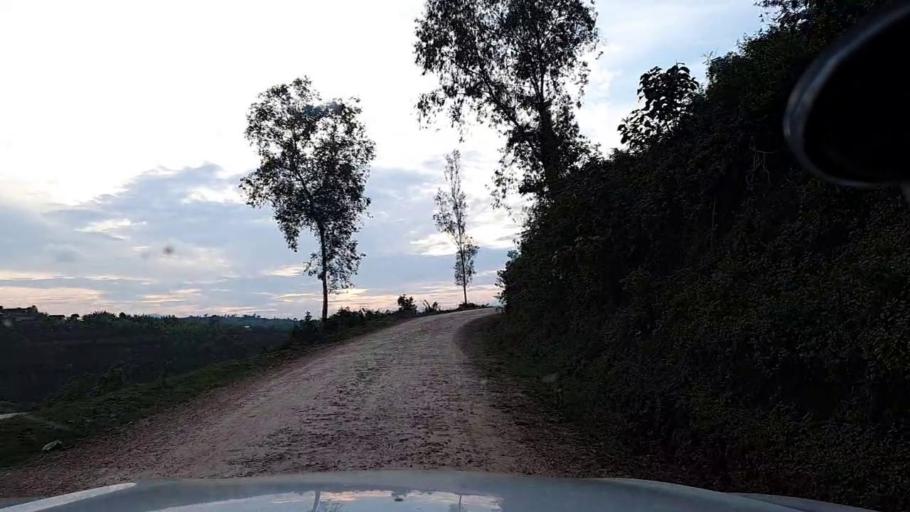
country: RW
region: Southern Province
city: Nyanza
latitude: -2.2143
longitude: 29.6280
